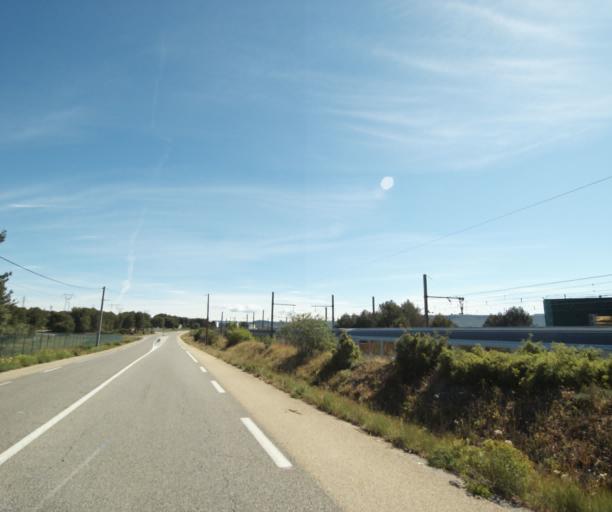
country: FR
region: Provence-Alpes-Cote d'Azur
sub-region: Departement des Bouches-du-Rhone
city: Rognac
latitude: 43.4981
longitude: 5.2072
